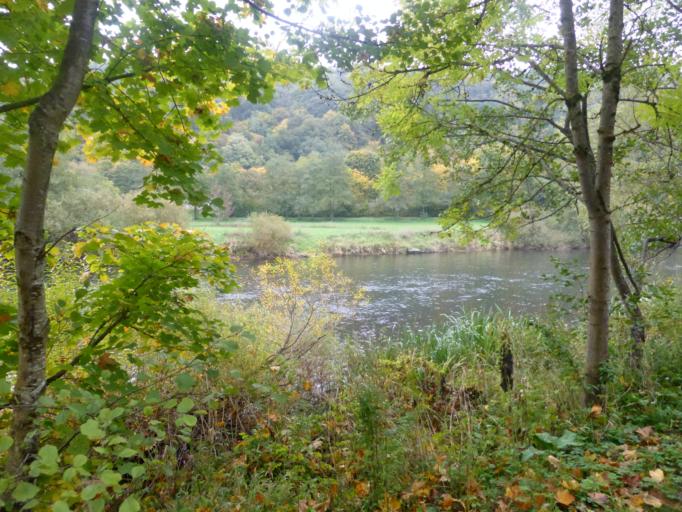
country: DE
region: Rheinland-Pfalz
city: Oberbillig
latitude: 49.7432
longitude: 6.5014
